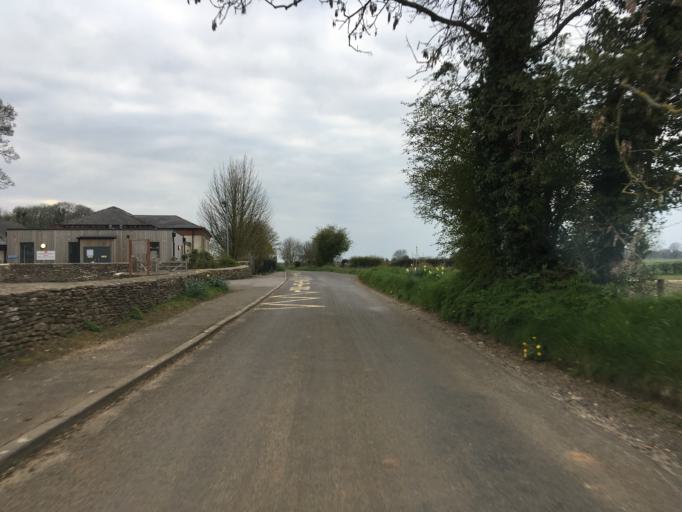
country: GB
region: England
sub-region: Wiltshire
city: Luckington
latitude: 51.6203
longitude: -2.2588
